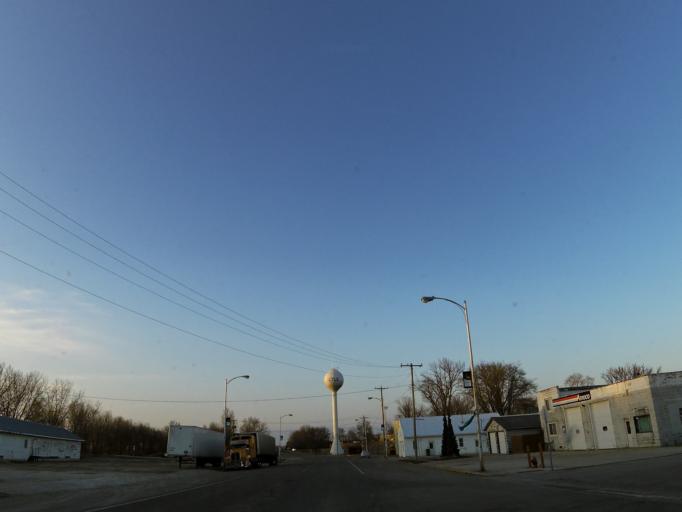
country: US
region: Iowa
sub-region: Mitchell County
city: Saint Ansgar
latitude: 43.5057
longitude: -92.9446
